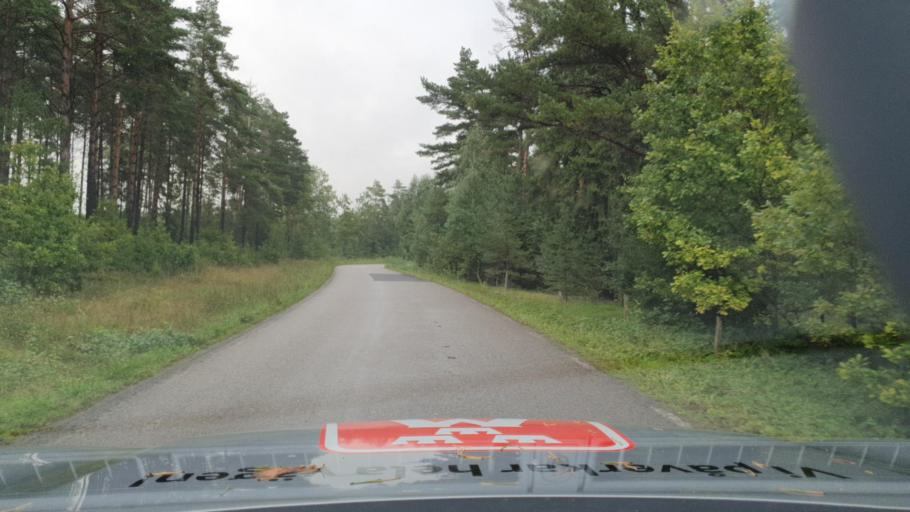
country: SE
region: Gotland
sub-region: Gotland
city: Visby
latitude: 57.6607
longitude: 18.5148
